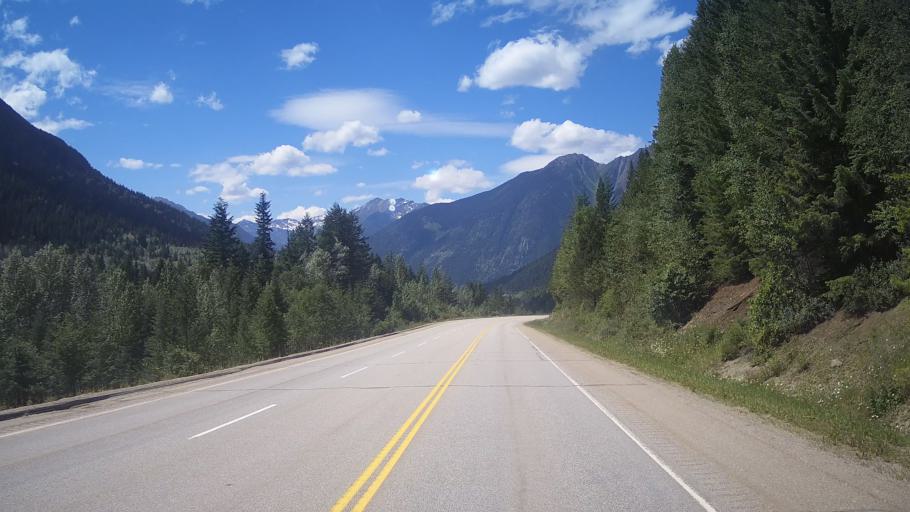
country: CA
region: Alberta
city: Grande Cache
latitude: 53.0263
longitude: -119.1608
